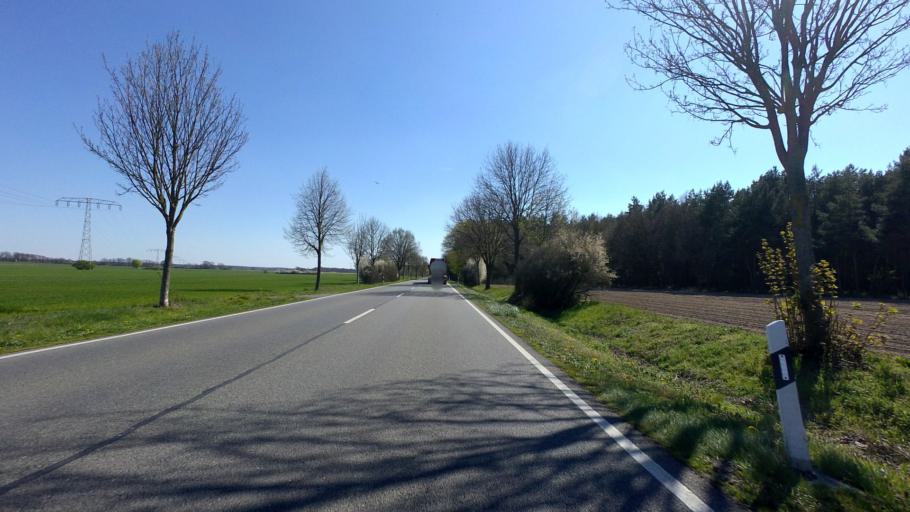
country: DE
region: Saxony-Anhalt
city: Pretzier
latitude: 52.7785
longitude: 11.2343
